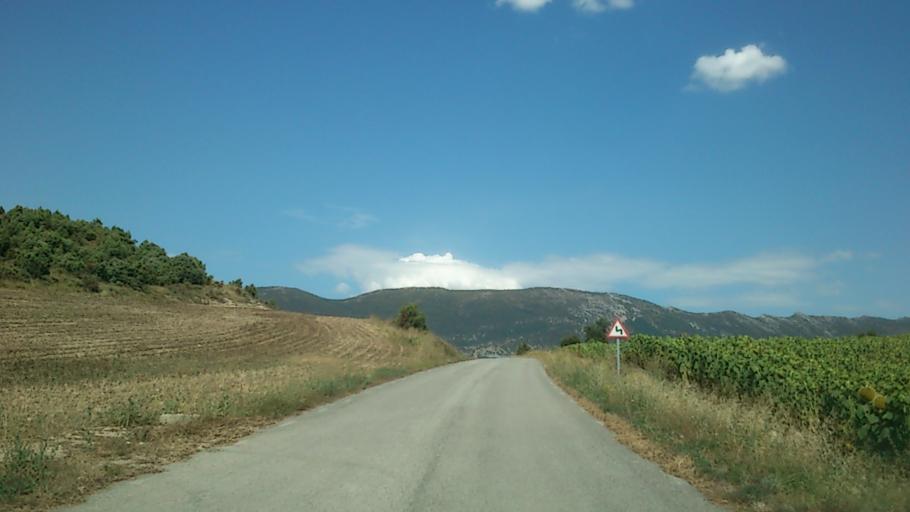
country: ES
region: Castille and Leon
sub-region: Provincia de Burgos
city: Frias
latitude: 42.8046
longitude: -3.2556
